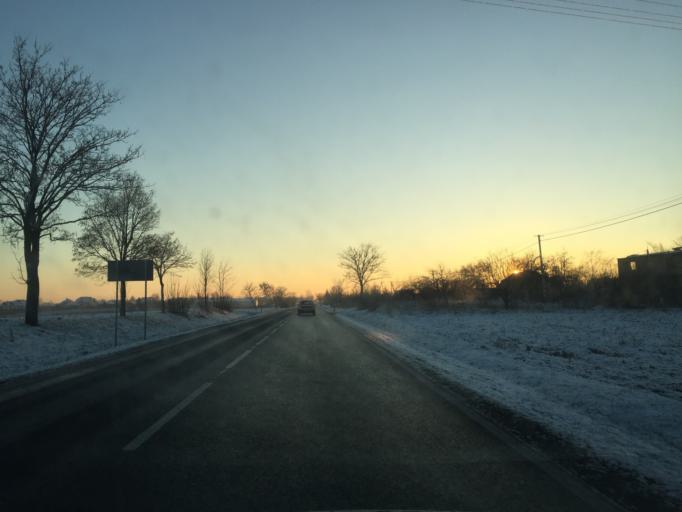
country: PL
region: Kujawsko-Pomorskie
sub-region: Powiat torunski
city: Lubicz Dolny
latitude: 53.0787
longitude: 18.7651
